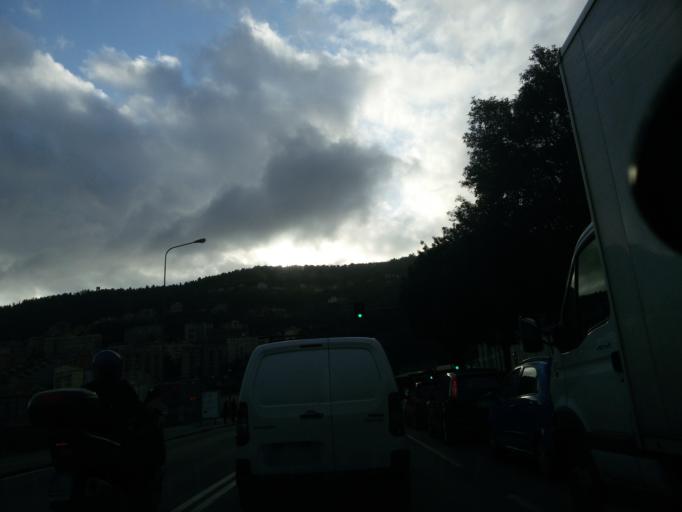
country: IT
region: Liguria
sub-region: Provincia di Genova
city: Genoa
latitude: 44.4281
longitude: 8.9508
